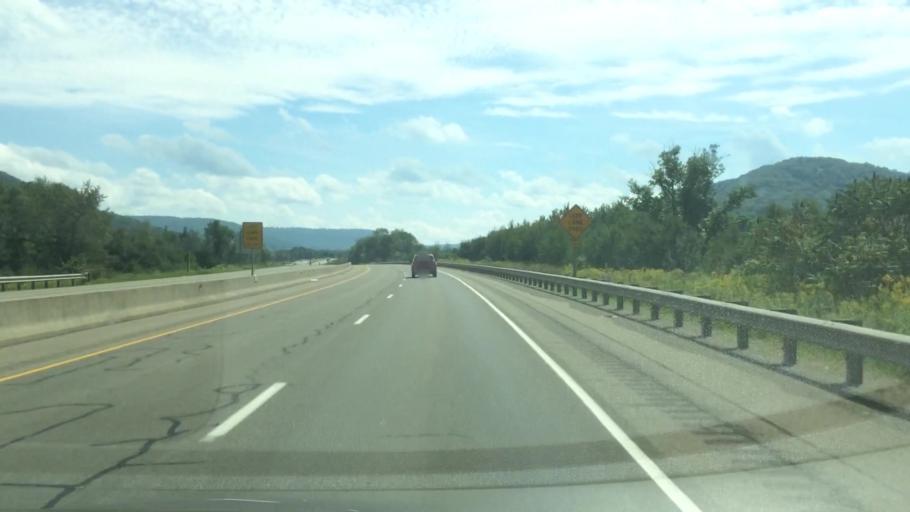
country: US
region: Pennsylvania
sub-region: McKean County
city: Bradford
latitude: 41.9381
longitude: -78.6497
